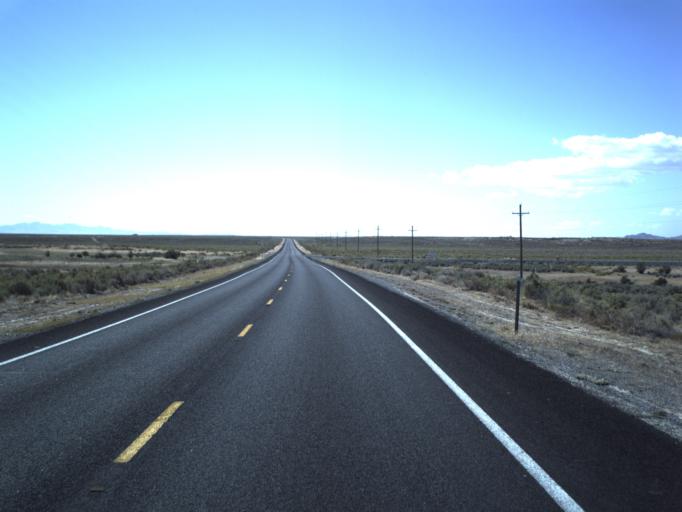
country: US
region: Utah
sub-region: Beaver County
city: Milford
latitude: 38.4581
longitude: -113.0049
